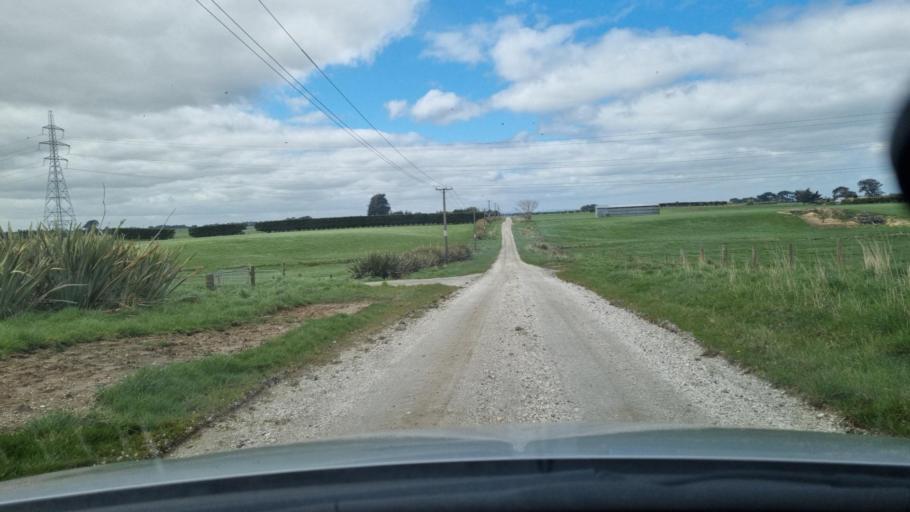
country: NZ
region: Southland
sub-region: Invercargill City
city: Invercargill
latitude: -46.4430
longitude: 168.4499
